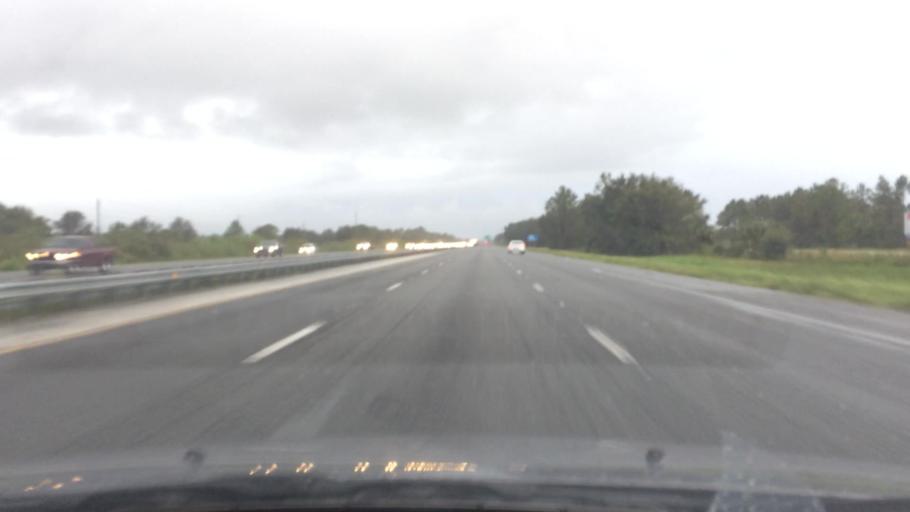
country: US
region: Florida
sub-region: Volusia County
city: Ormond-by-the-Sea
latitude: 29.3154
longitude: -81.1315
